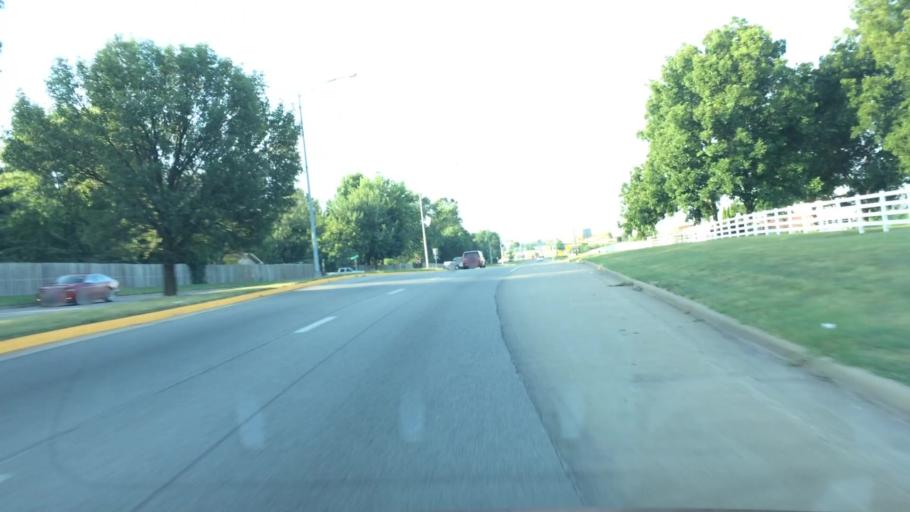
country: US
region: Missouri
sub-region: Greene County
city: Springfield
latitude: 37.1727
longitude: -93.3161
